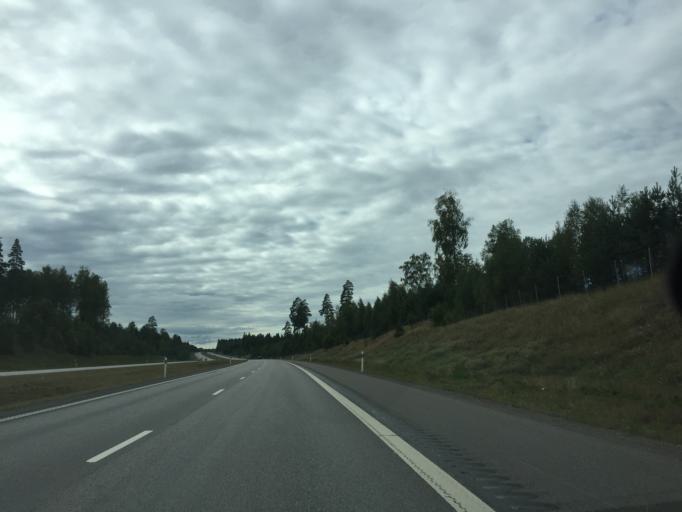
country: SE
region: OErebro
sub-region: Lindesbergs Kommun
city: Fellingsbro
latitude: 59.3678
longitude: 15.5790
